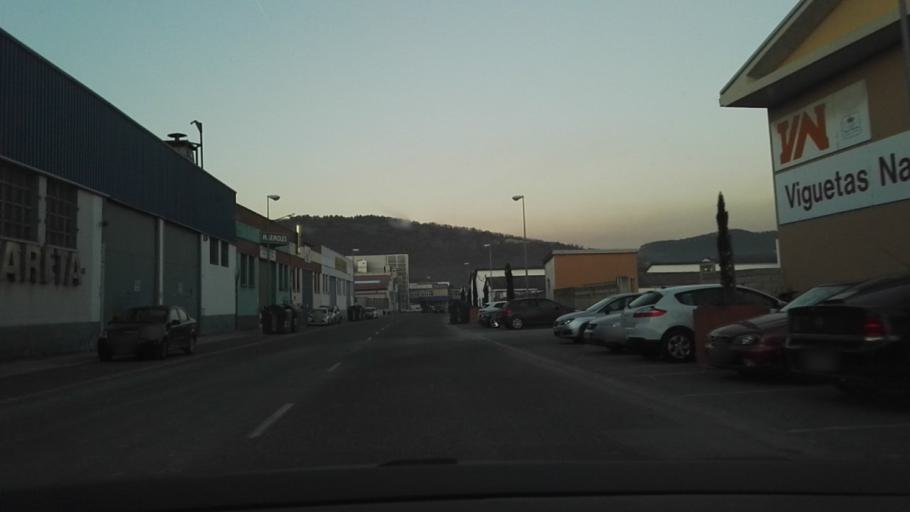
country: ES
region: Navarre
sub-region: Provincia de Navarra
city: Atarrabia
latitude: 42.8250
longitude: -1.6015
